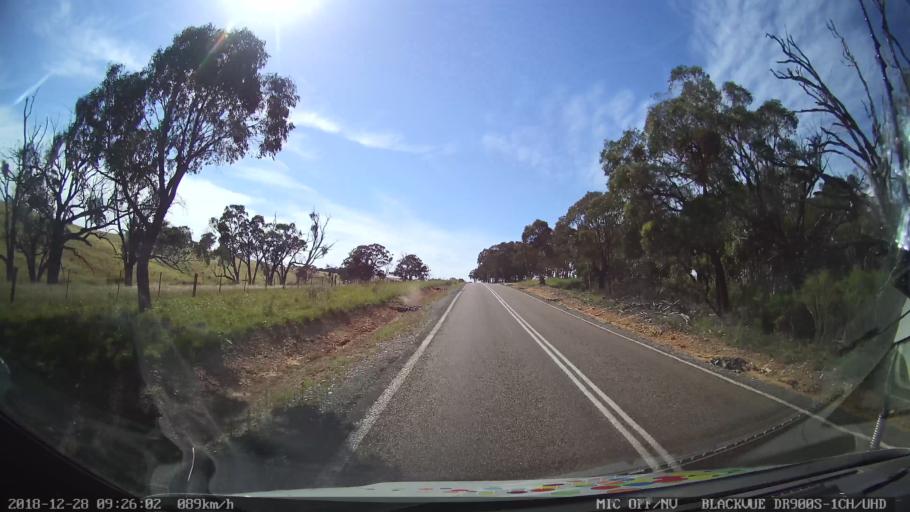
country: AU
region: New South Wales
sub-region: Upper Lachlan Shire
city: Crookwell
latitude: -34.4154
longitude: 149.3958
